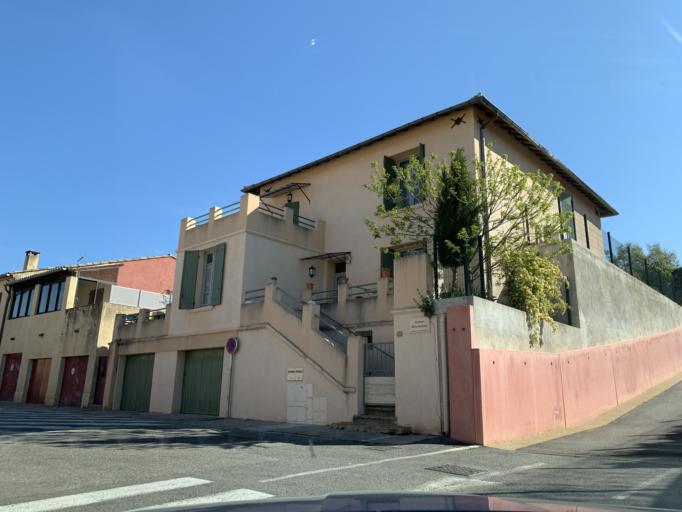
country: FR
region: Provence-Alpes-Cote d'Azur
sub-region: Departement du Vaucluse
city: Roussillon
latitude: 43.9002
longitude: 5.2942
